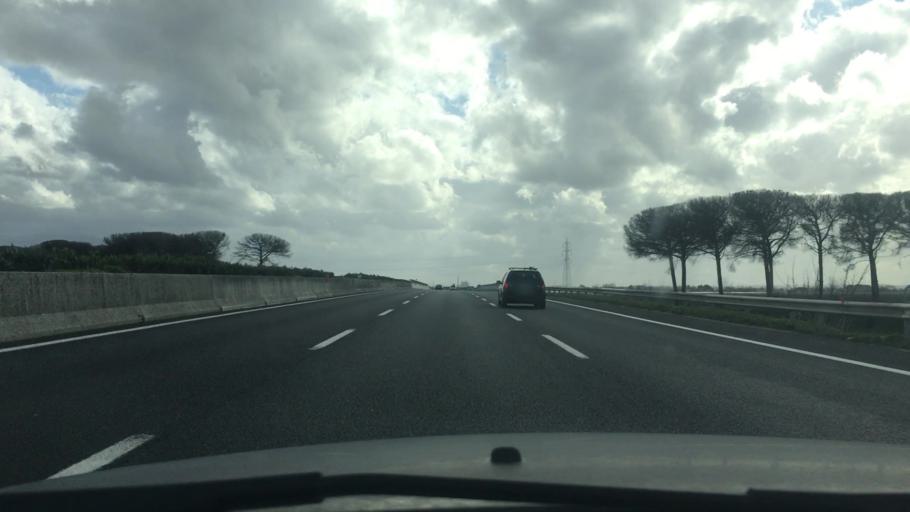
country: IT
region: Campania
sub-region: Provincia di Napoli
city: Pascarola
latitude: 40.9875
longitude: 14.3250
